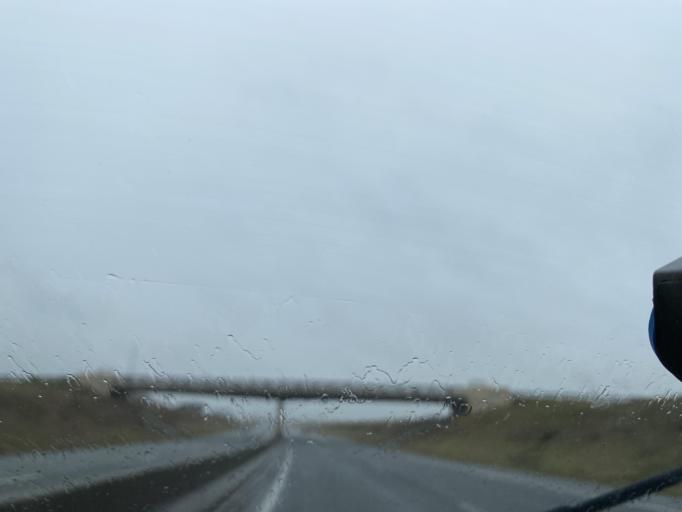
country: FR
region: Centre
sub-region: Departement d'Eure-et-Loir
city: Villemeux-sur-Eure
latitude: 48.5845
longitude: 1.4282
